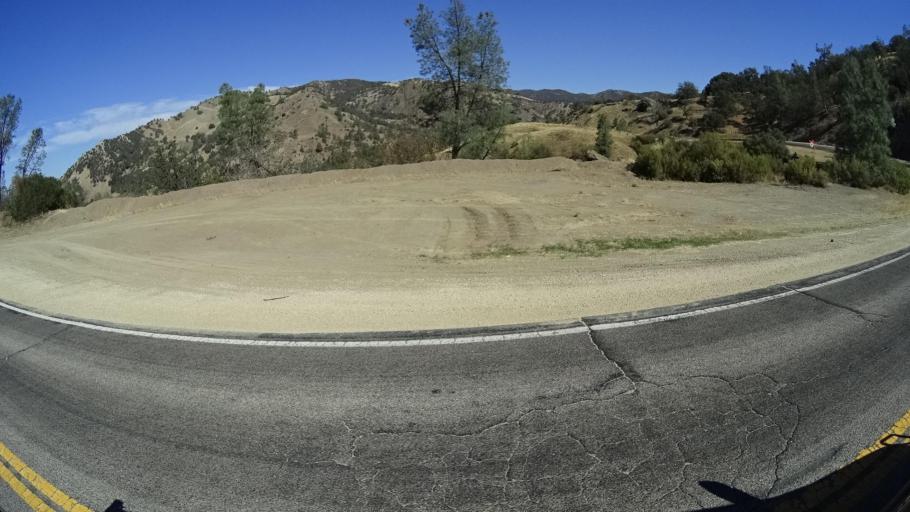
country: US
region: California
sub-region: Fresno County
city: Coalinga
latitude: 36.1956
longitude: -120.7398
